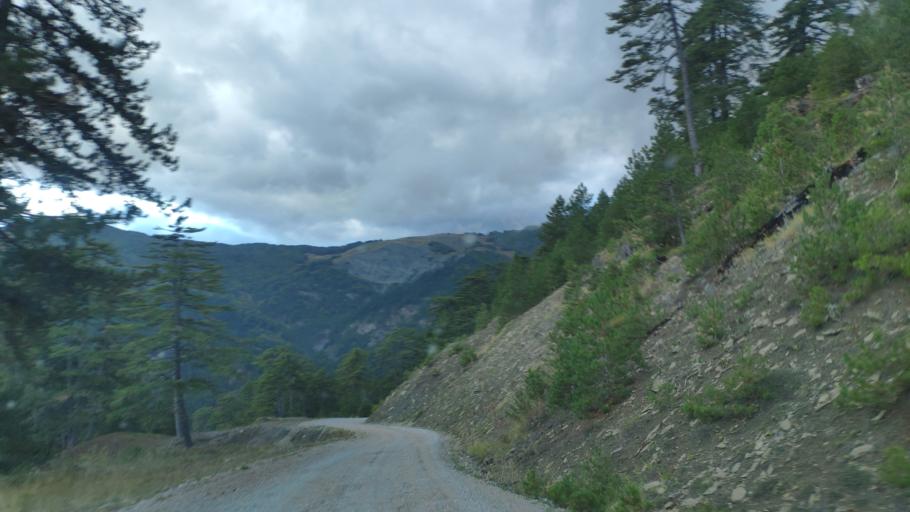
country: AL
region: Korce
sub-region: Rrethi i Kolonjes
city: Erseke
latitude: 40.2900
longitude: 20.8618
